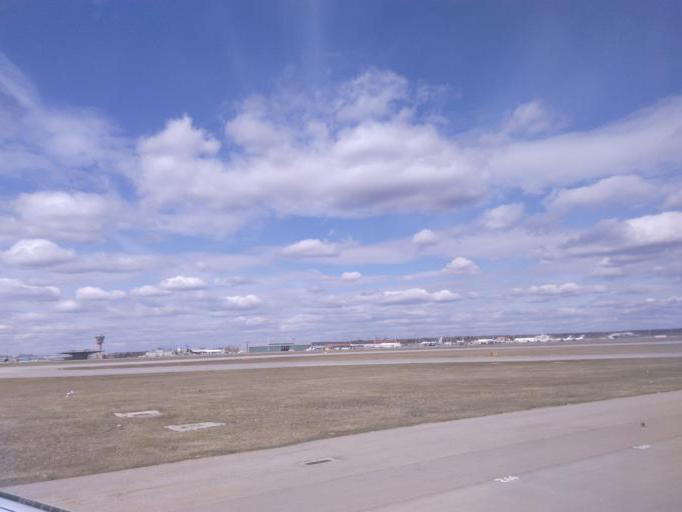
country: RU
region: Moscow
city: Khimki
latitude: 55.9698
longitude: 37.4181
